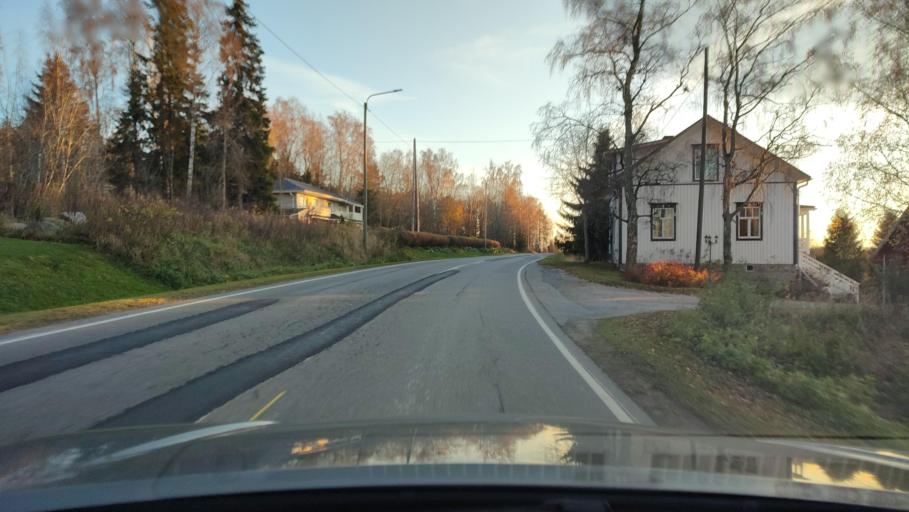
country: FI
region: Ostrobothnia
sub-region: Sydosterbotten
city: Naerpes
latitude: 62.4309
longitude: 21.3478
